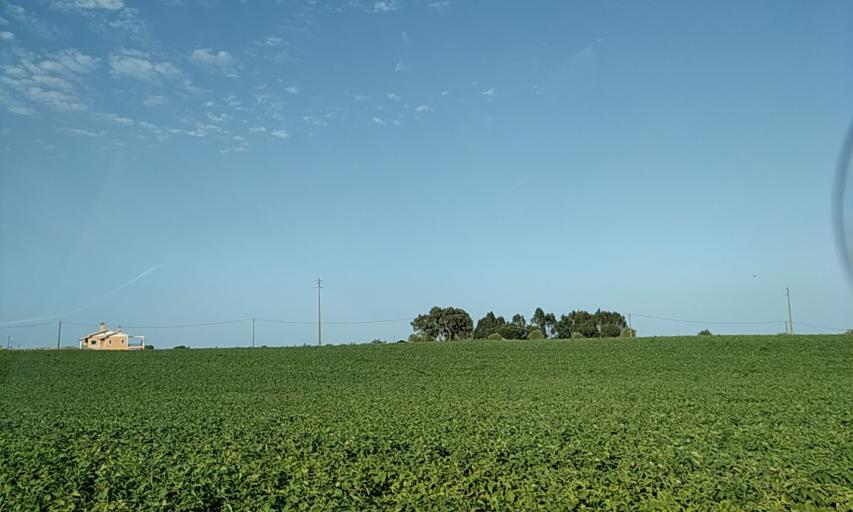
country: PT
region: Santarem
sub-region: Santarem
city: Santarem
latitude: 39.3452
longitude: -8.6611
